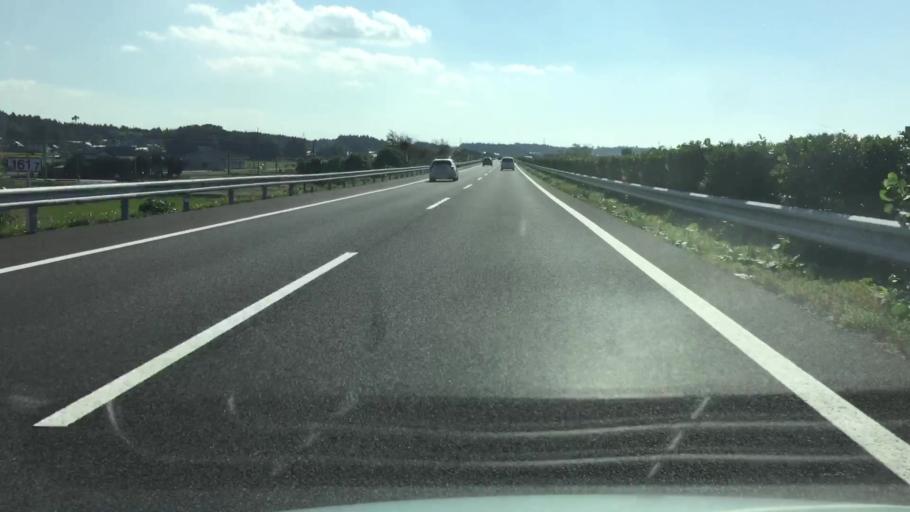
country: JP
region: Ibaraki
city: Tomobe
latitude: 36.3249
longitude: 140.2992
